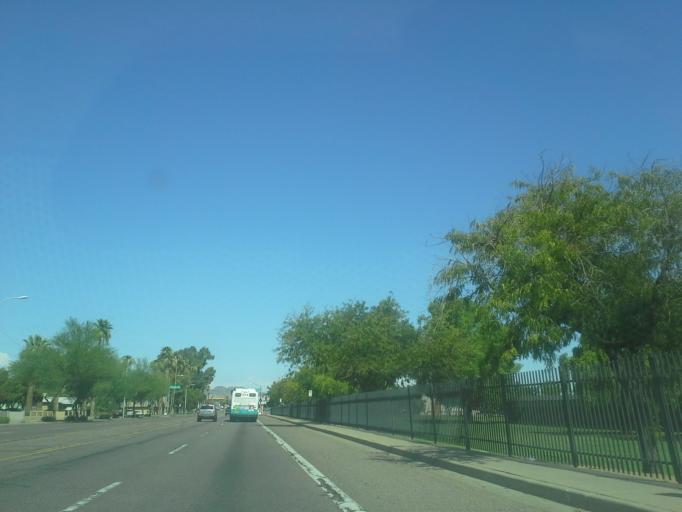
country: US
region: Arizona
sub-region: Maricopa County
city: Glendale
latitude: 33.5386
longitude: -112.1058
